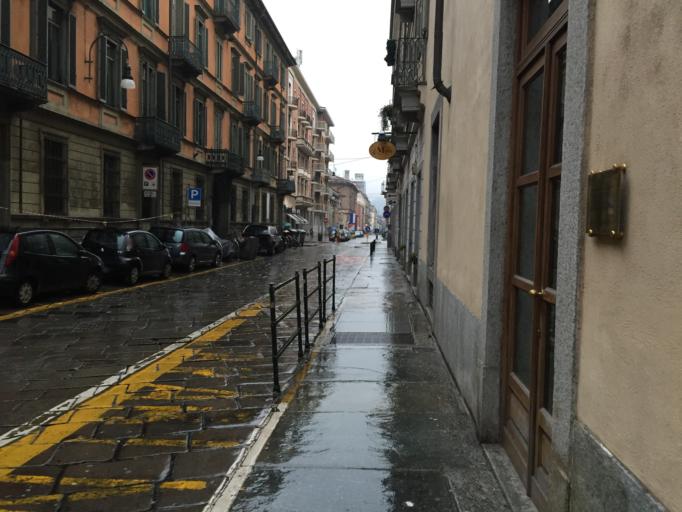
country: IT
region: Piedmont
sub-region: Provincia di Torino
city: Turin
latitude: 45.0692
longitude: 7.6901
